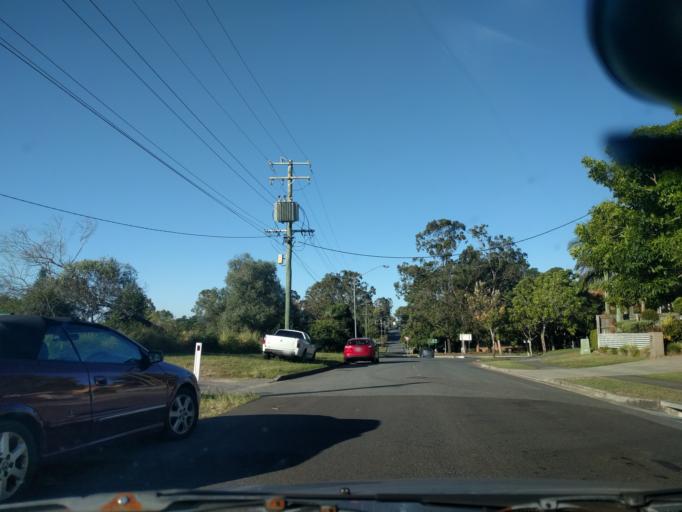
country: AU
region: Queensland
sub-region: Brisbane
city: Richlands
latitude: -27.6011
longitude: 152.9491
